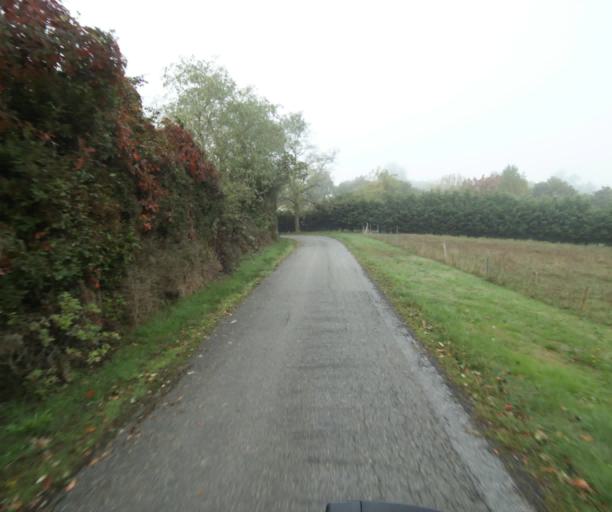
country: FR
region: Midi-Pyrenees
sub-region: Departement du Tarn-et-Garonne
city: Saint-Nauphary
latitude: 43.9353
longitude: 1.4647
